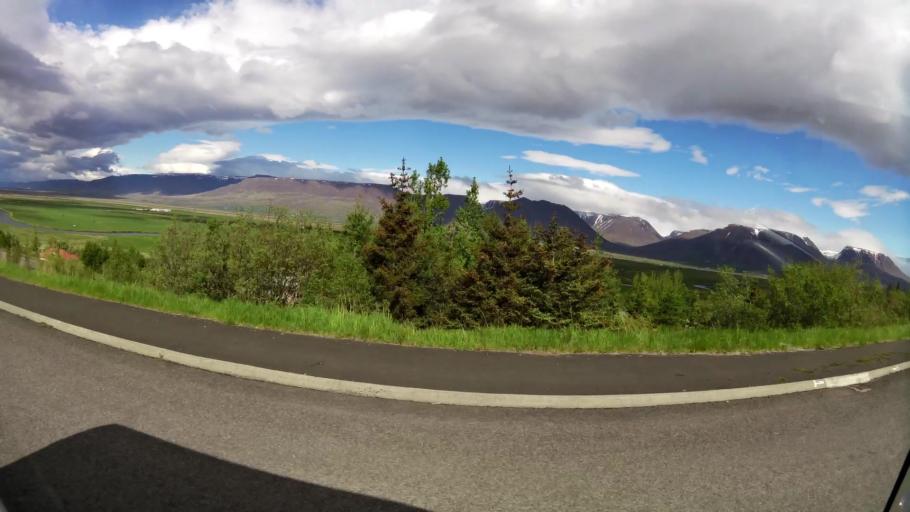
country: IS
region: Northwest
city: Saudarkrokur
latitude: 65.5524
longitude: -19.4493
